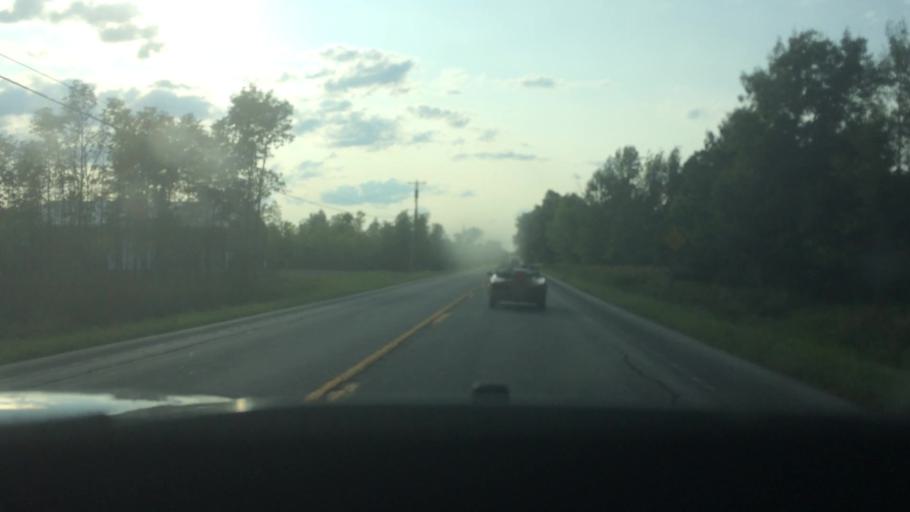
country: US
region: New York
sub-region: St. Lawrence County
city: Canton
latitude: 44.6506
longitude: -75.2983
